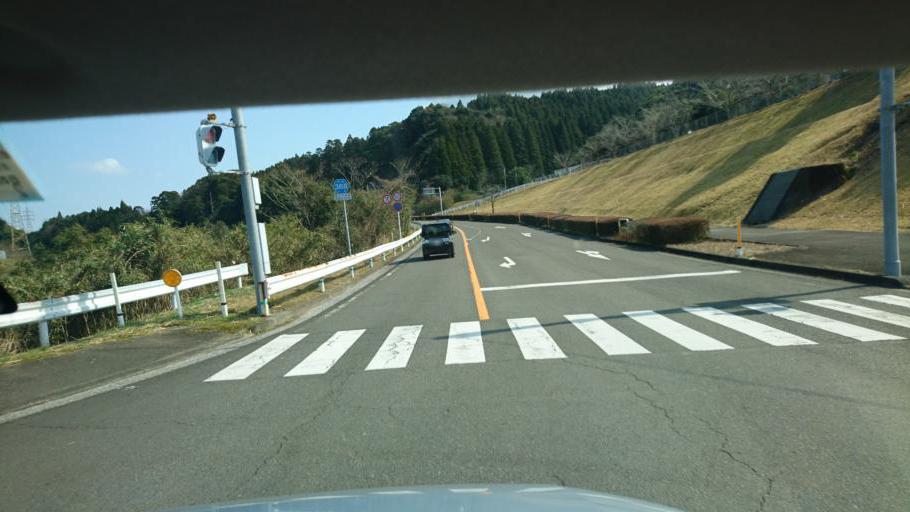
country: JP
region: Miyazaki
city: Miyazaki-shi
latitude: 31.8360
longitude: 131.4015
